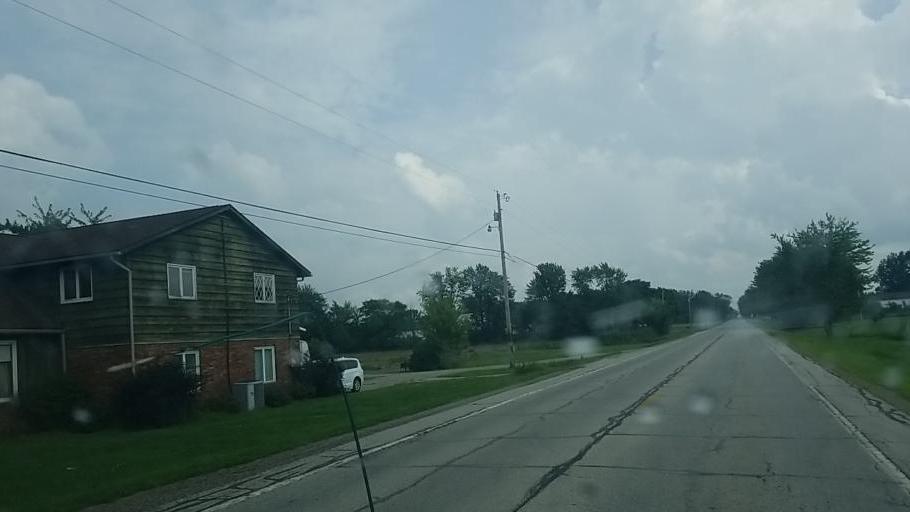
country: US
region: Ohio
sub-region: Lorain County
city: Lagrange
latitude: 41.1680
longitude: -82.0610
